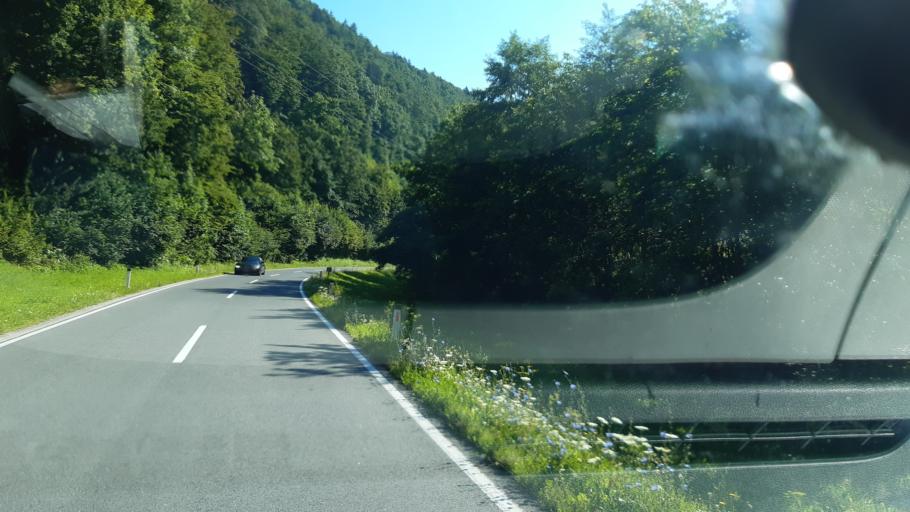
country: SI
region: Vransko
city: Vransko
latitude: 46.2230
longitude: 14.9160
